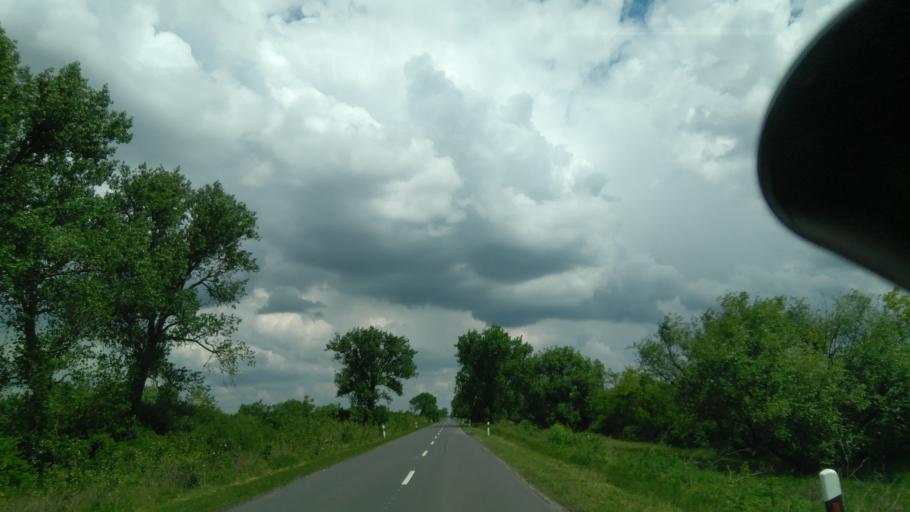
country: HU
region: Bekes
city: Devavanya
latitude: 47.0065
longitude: 20.9195
